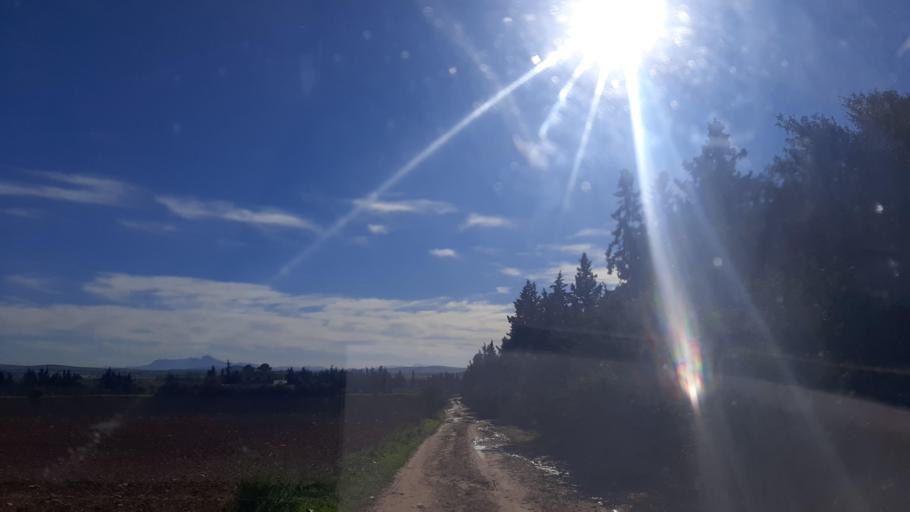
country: TN
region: Tunis
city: Oued Lill
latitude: 36.7607
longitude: 9.9820
